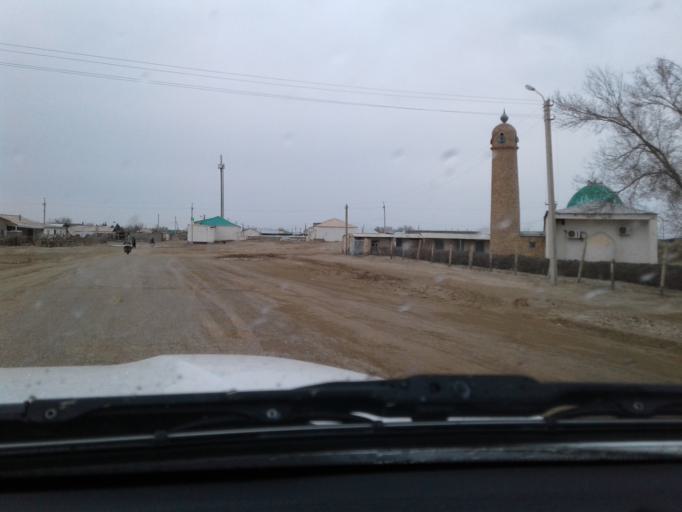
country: TM
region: Ahal
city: Abadan
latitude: 38.7604
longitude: 58.4921
